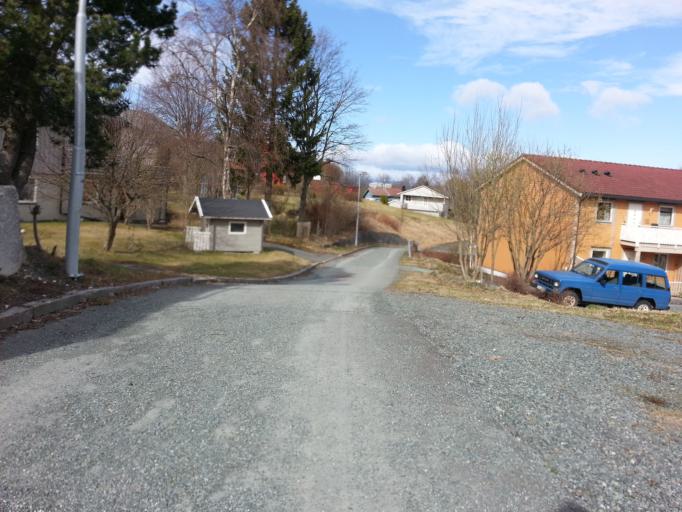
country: NO
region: Sor-Trondelag
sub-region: Trondheim
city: Trondheim
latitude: 63.4069
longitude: 10.4120
